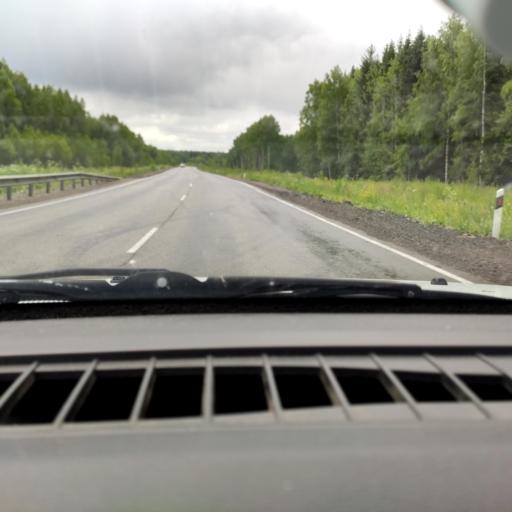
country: RU
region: Perm
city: Kungur
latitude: 57.3407
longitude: 56.9674
